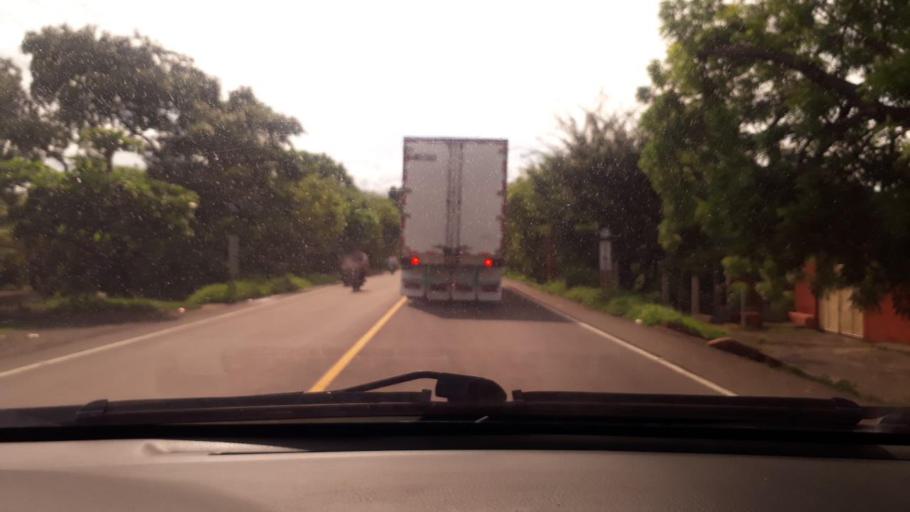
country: SV
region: Ahuachapan
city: San Francisco Menendez
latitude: 13.8795
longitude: -90.1132
